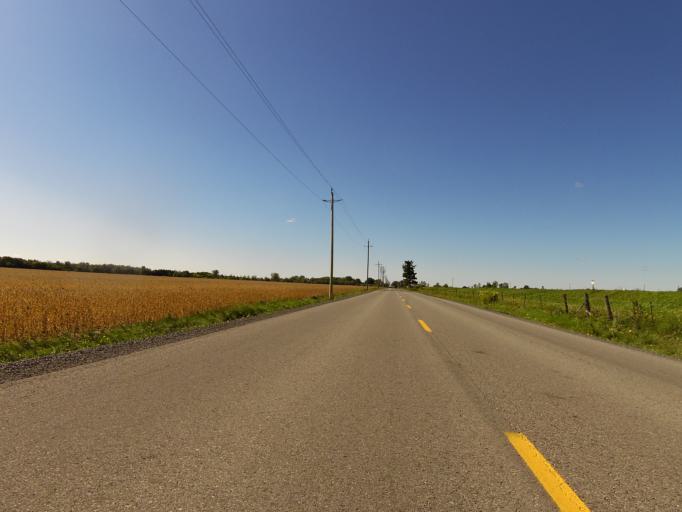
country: CA
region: Ontario
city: Casselman
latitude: 45.2728
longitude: -75.2397
